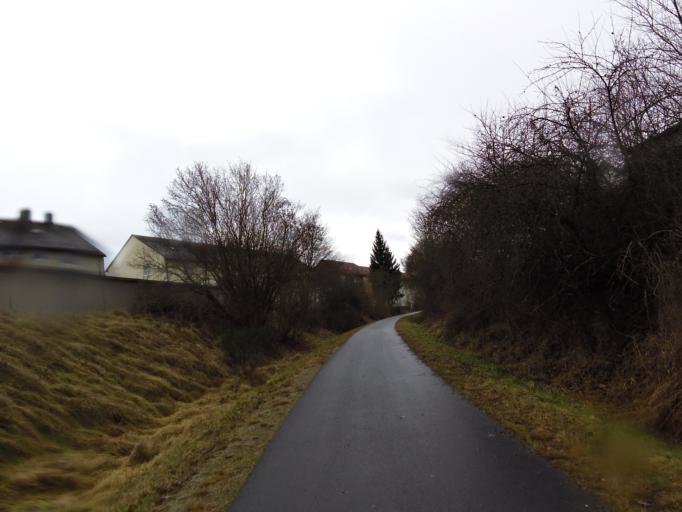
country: DE
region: Bavaria
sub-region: Upper Franconia
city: Wunsiedel
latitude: 50.0414
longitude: 12.0091
